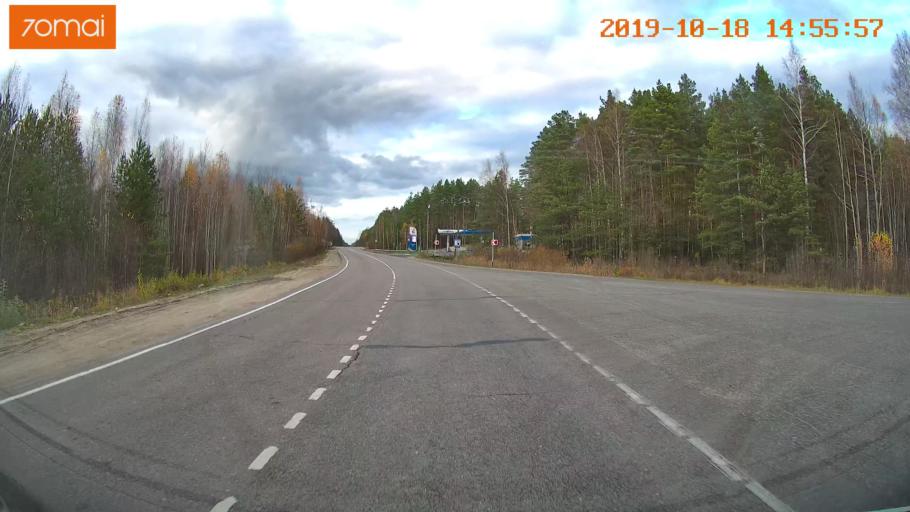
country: RU
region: Vladimir
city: Kurlovo
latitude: 55.4588
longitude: 40.5896
